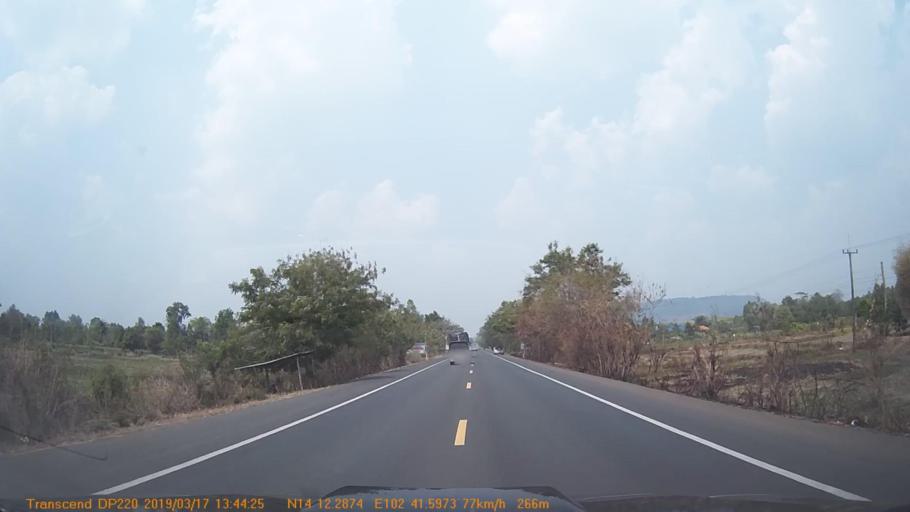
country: TH
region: Buriram
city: Non Din Daeng
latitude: 14.2051
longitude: 102.6934
